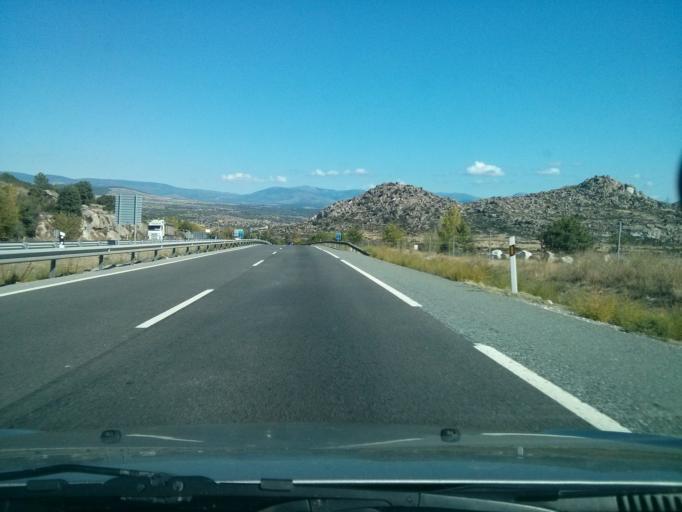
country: ES
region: Madrid
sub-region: Provincia de Madrid
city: La Cabrera
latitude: 40.8787
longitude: -3.5993
